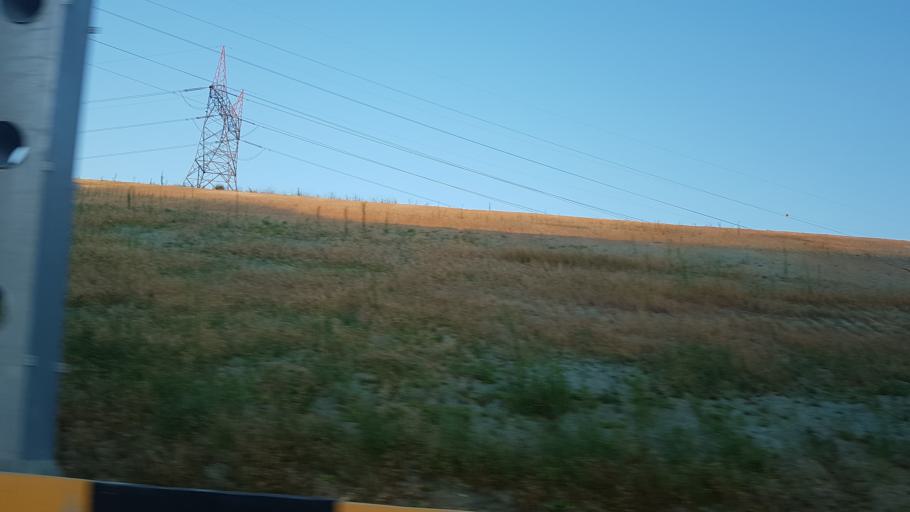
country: TR
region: Kocaeli
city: Tavsanli
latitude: 40.8058
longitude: 29.5200
